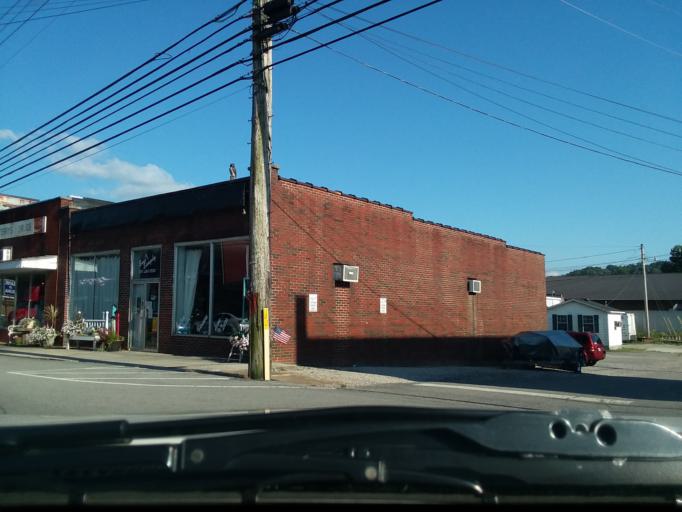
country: US
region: Tennessee
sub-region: Clay County
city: Celina
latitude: 36.5502
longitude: -85.5060
